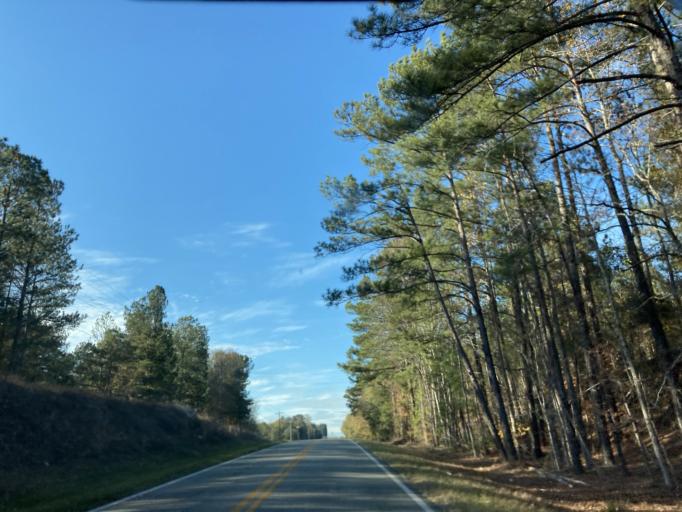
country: US
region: Georgia
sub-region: Jones County
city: Gray
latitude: 32.8904
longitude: -83.5047
